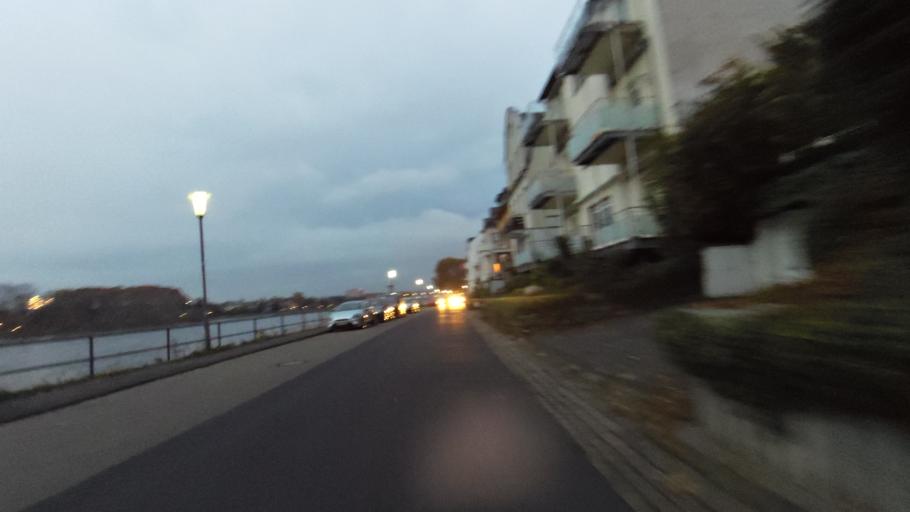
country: DE
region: Rheinland-Pfalz
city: Koblenz
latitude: 50.3412
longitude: 7.5991
